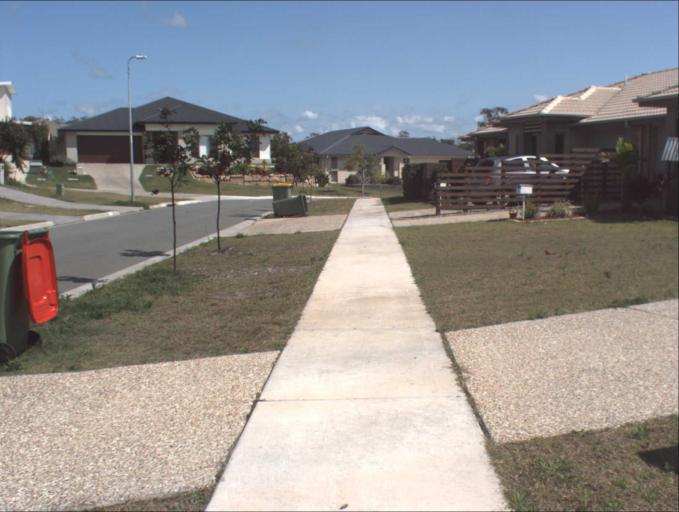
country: AU
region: Queensland
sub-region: Logan
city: Chambers Flat
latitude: -27.8042
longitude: 153.1060
